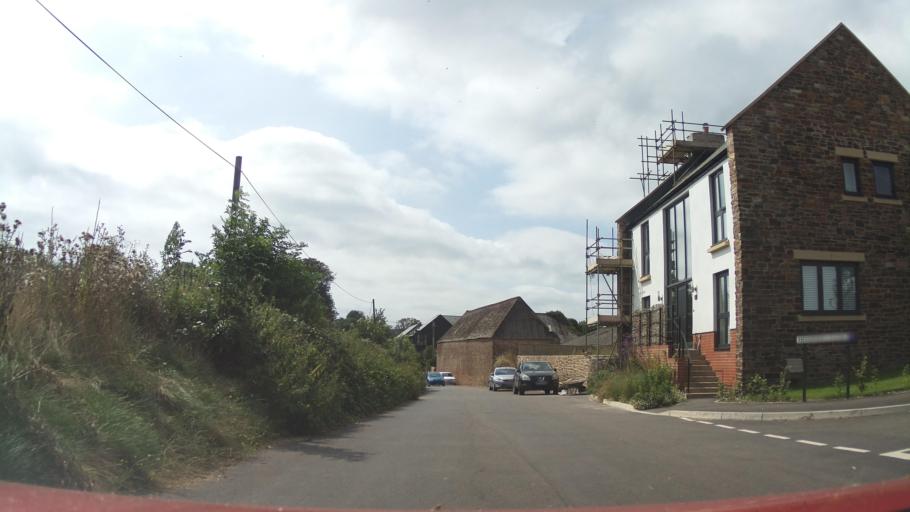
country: GB
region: England
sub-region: Devon
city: Totnes
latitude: 50.4308
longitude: -3.6643
